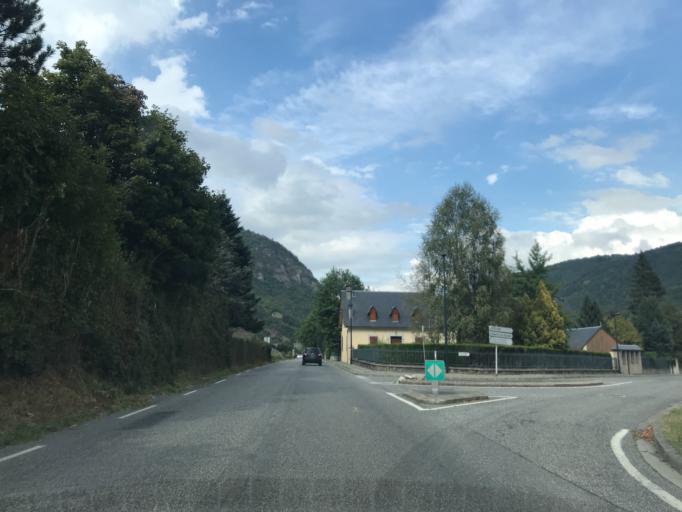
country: FR
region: Midi-Pyrenees
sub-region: Departement des Hautes-Pyrenees
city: Saint-Lary-Soulan
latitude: 42.8653
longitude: 0.3391
